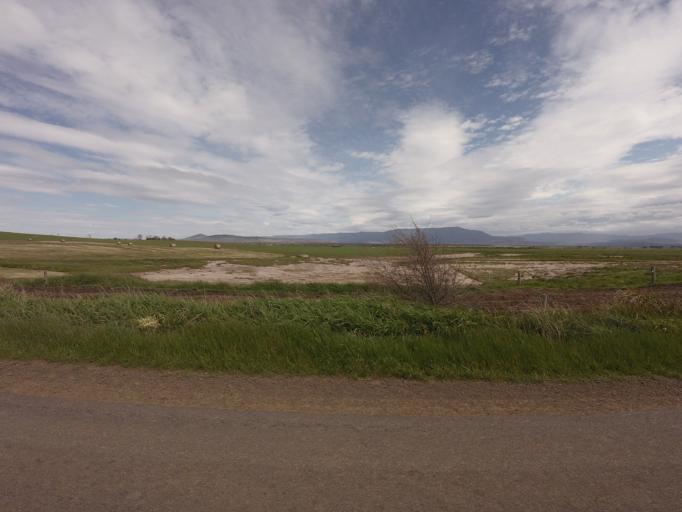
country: AU
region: Tasmania
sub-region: Northern Midlands
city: Evandale
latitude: -41.8222
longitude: 147.3127
